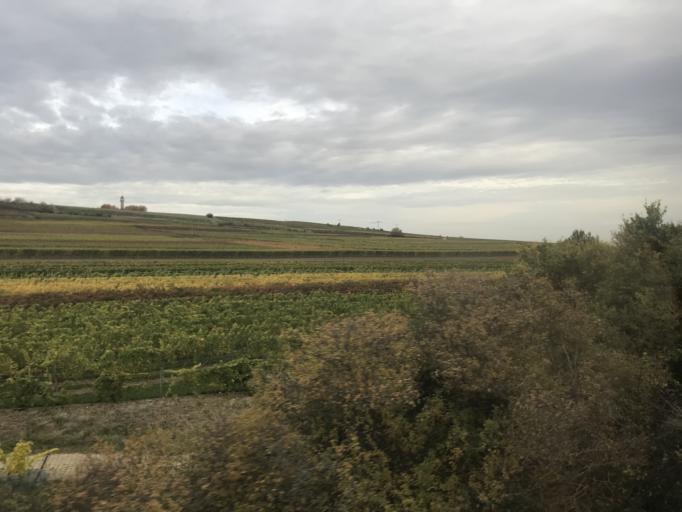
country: DE
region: Rheinland-Pfalz
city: Kettenheim
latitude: 49.7265
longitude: 8.1133
